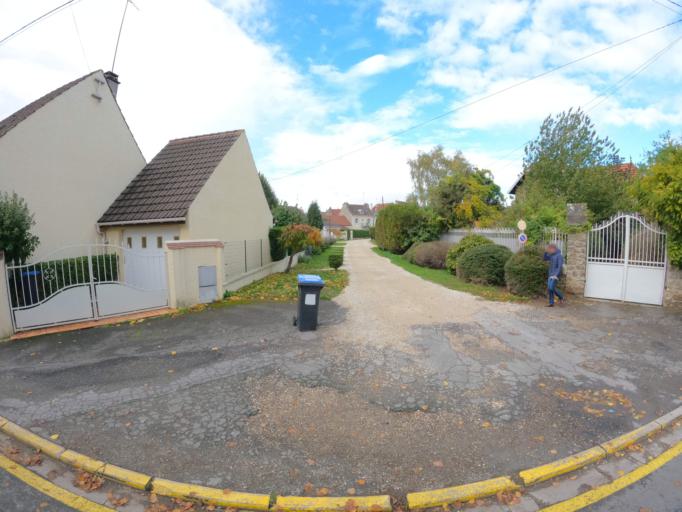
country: FR
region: Ile-de-France
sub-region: Departement de Seine-et-Marne
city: Saint-Germain-sur-Morin
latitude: 48.8826
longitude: 2.8537
